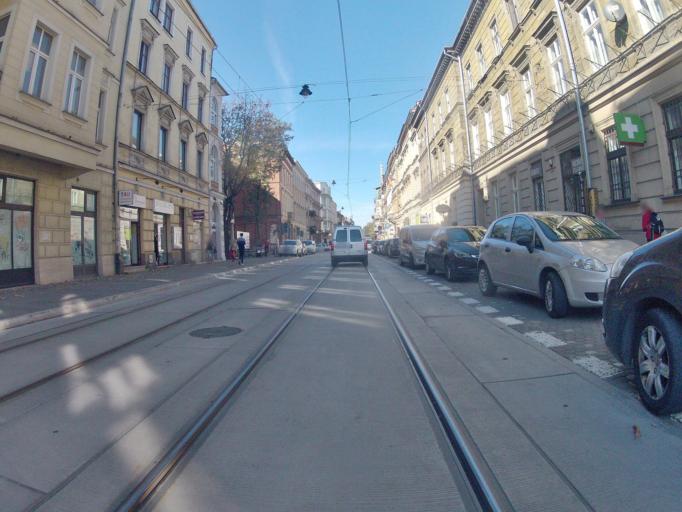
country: PL
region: Lesser Poland Voivodeship
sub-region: Krakow
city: Krakow
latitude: 50.0658
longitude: 19.9304
